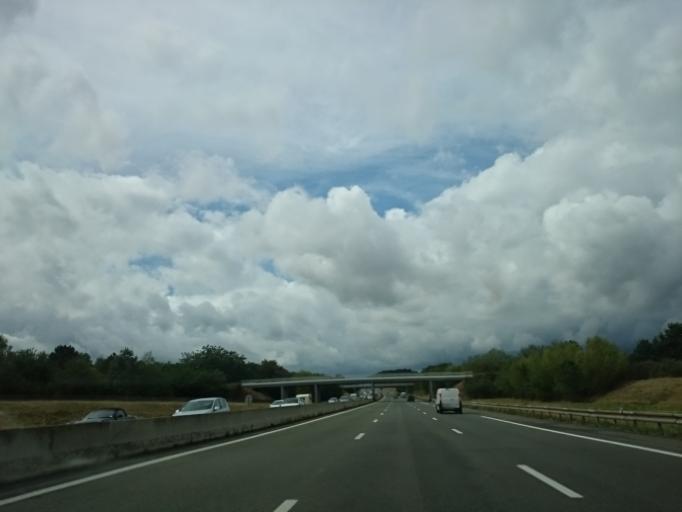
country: FR
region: Pays de la Loire
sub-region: Departement de la Sarthe
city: Champagne
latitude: 48.0505
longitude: 0.2959
